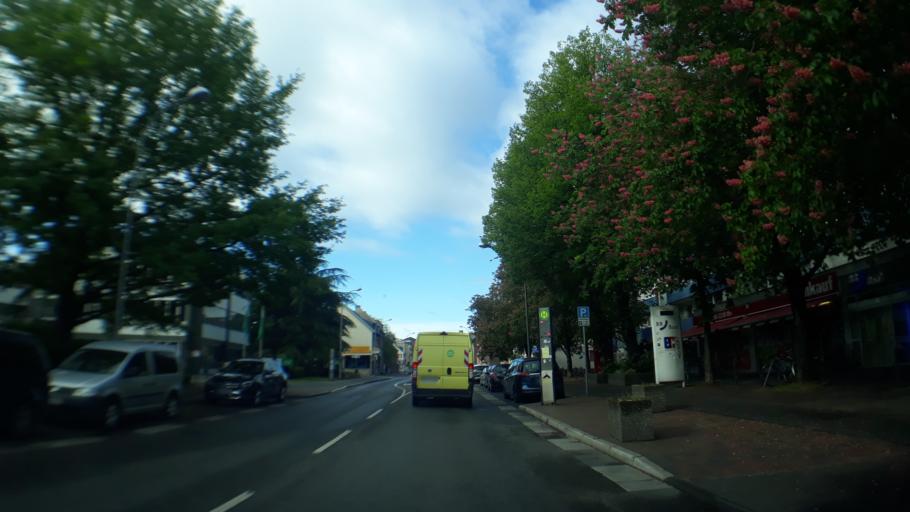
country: DE
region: North Rhine-Westphalia
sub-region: Regierungsbezirk Koln
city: Hurth
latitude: 50.8797
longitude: 6.8899
